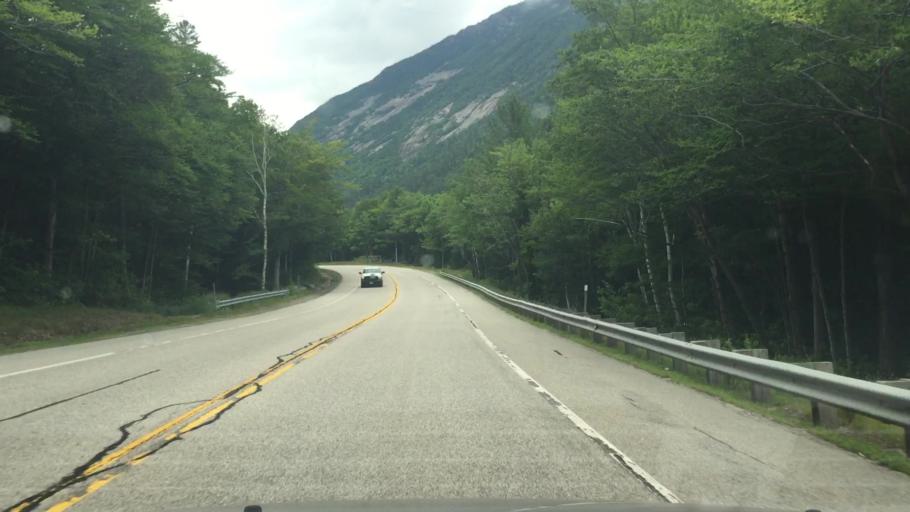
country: US
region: New Hampshire
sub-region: Grafton County
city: Deerfield
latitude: 44.1748
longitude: -71.3940
